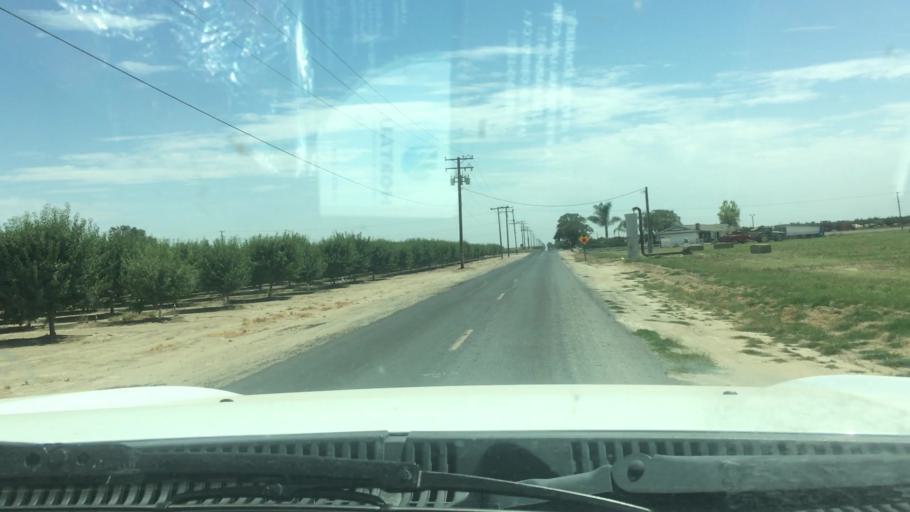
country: US
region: California
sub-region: Tulare County
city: Tipton
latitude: 36.0536
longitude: -119.3220
